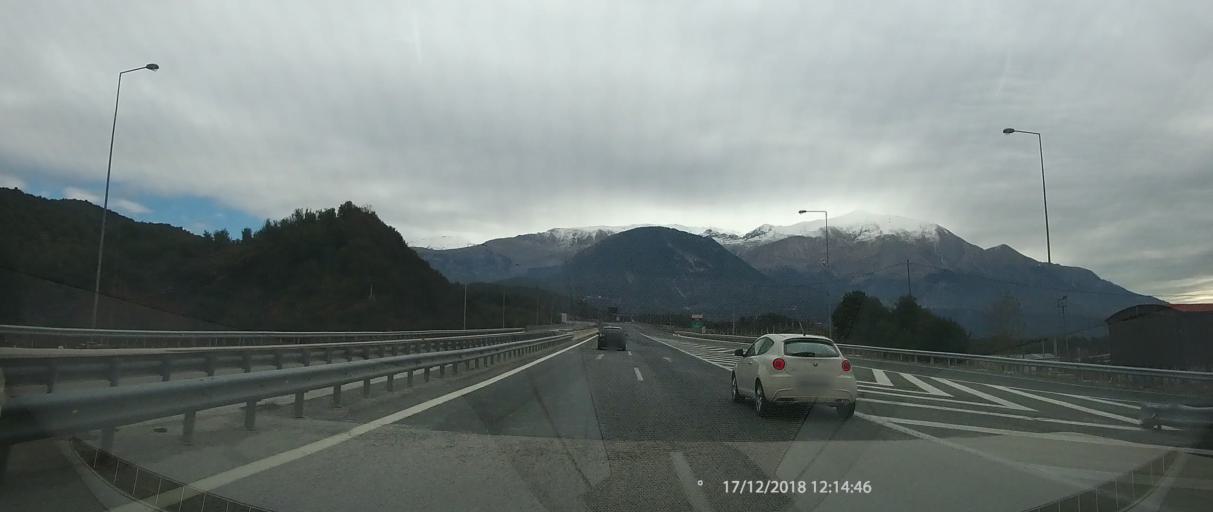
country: GR
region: Epirus
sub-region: Nomos Ioanninon
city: Katsikas
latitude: 39.7169
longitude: 21.0056
